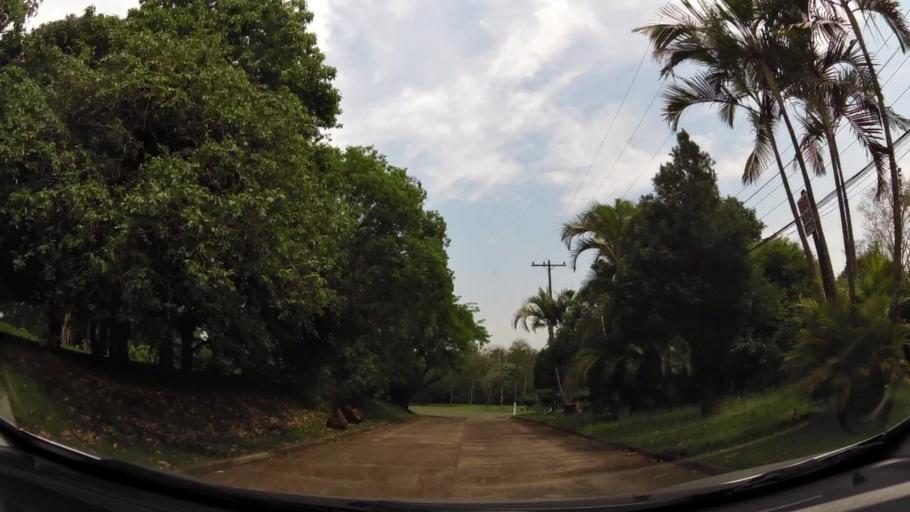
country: PY
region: Alto Parana
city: Ciudad del Este
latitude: -25.4903
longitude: -54.6073
